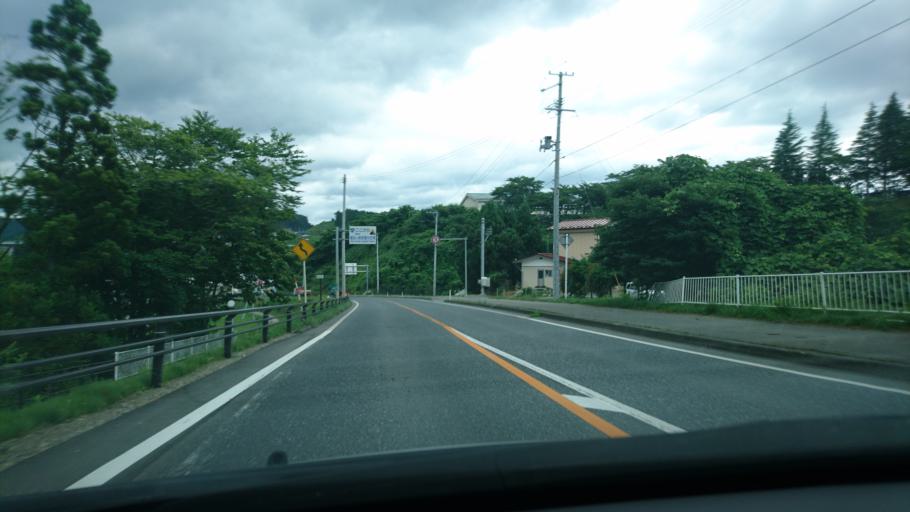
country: JP
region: Iwate
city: Ofunato
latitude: 38.9878
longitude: 141.6157
